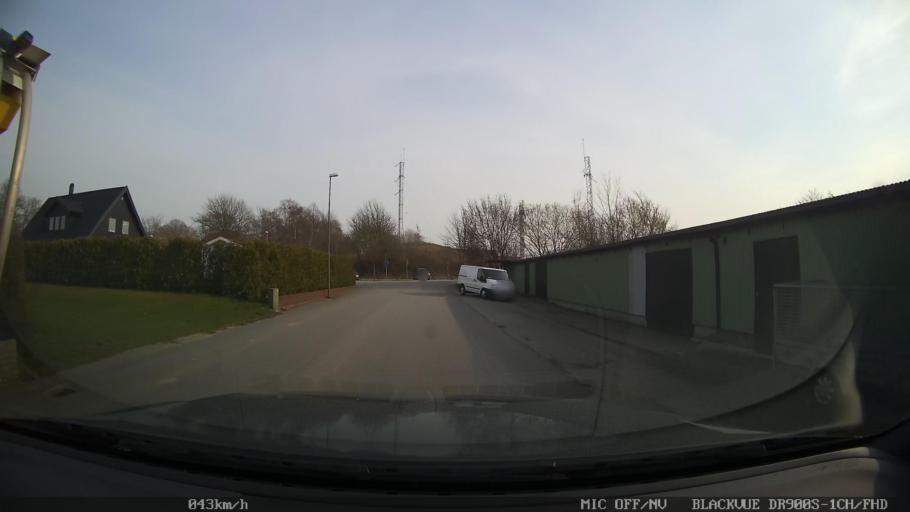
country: SE
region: Skane
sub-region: Ystads Kommun
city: Ystad
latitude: 55.4508
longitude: 13.7957
